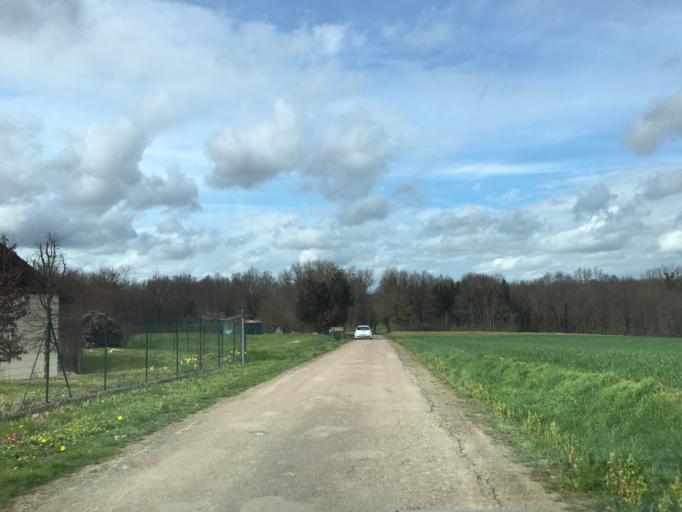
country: FR
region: Bourgogne
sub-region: Departement de l'Yonne
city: Fleury-la-Vallee
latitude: 47.8637
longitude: 3.4081
